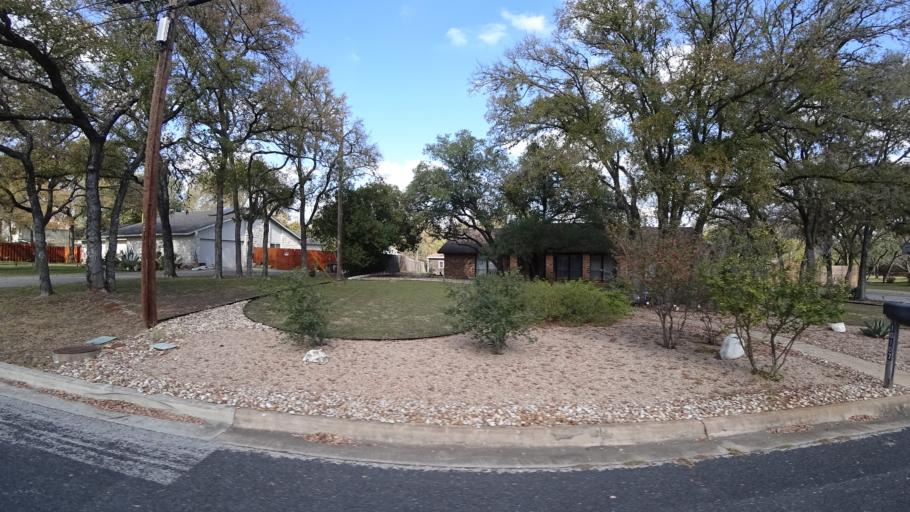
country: US
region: Texas
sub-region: Travis County
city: Shady Hollow
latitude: 30.1806
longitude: -97.8502
